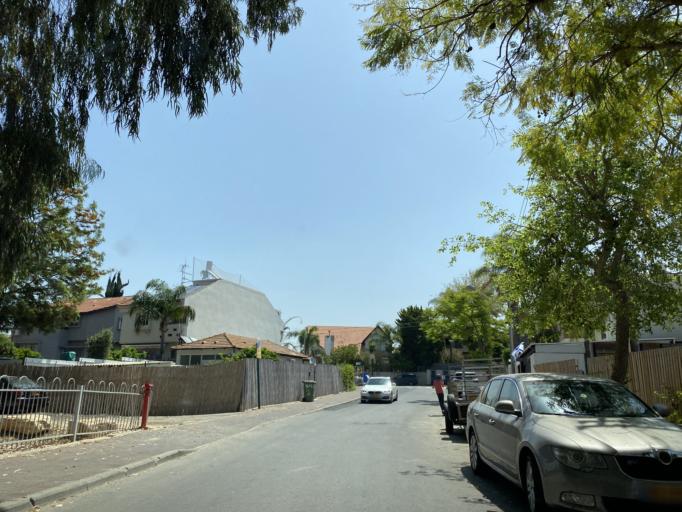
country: IL
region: Central District
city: Ra'anana
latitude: 32.1900
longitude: 34.8700
